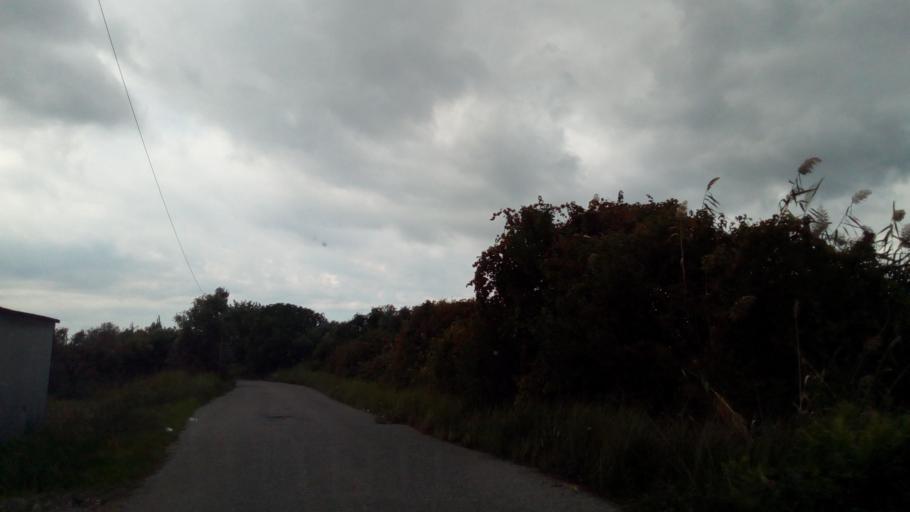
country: GR
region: West Greece
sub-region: Nomos Aitolias kai Akarnanias
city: Nafpaktos
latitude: 38.4027
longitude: 21.9145
